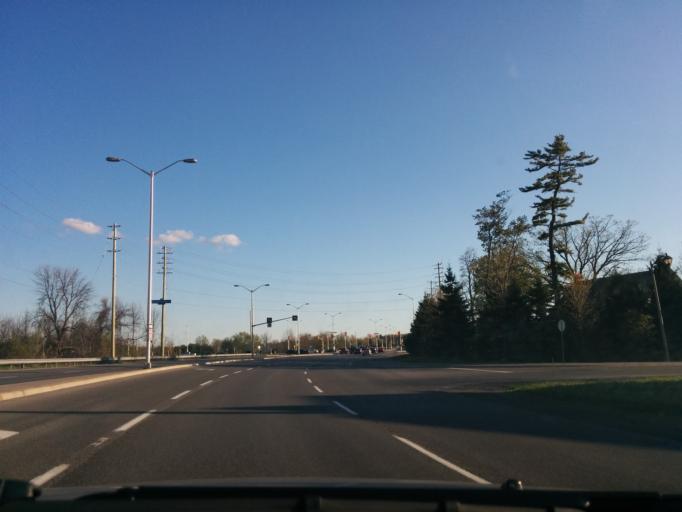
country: CA
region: Ontario
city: Bells Corners
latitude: 45.2727
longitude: -75.7043
